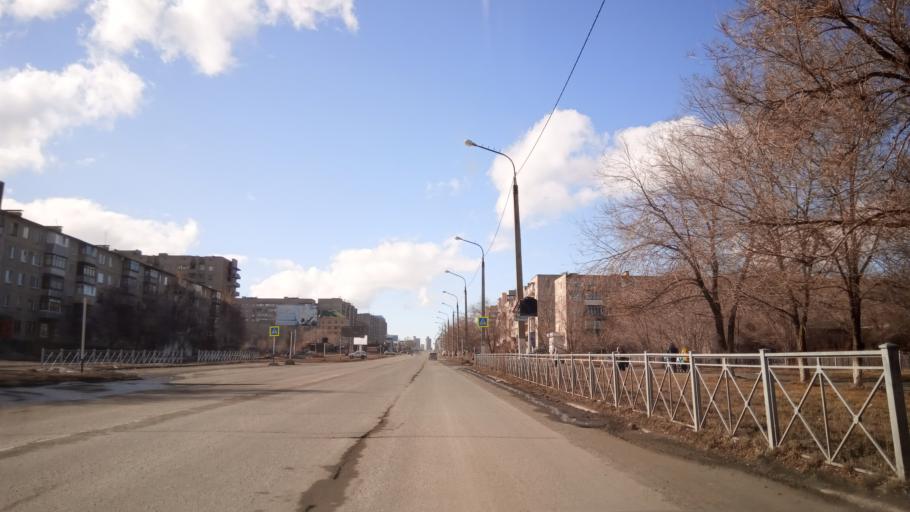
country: RU
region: Orenburg
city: Novotroitsk
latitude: 51.1843
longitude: 58.2814
